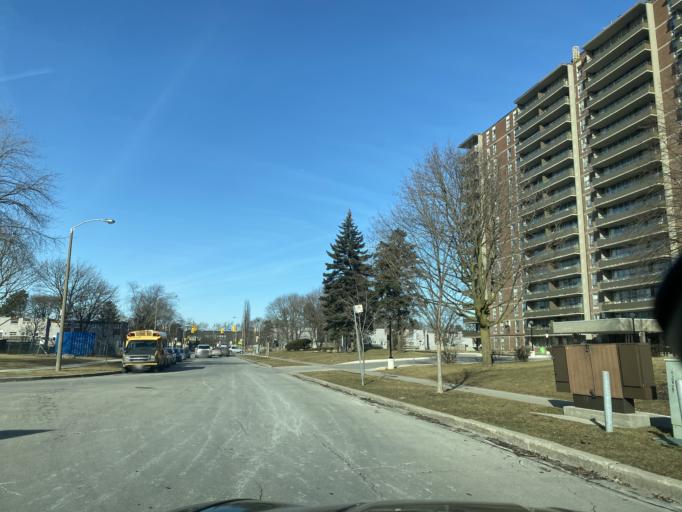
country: CA
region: Ontario
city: Scarborough
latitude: 43.7830
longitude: -79.2967
